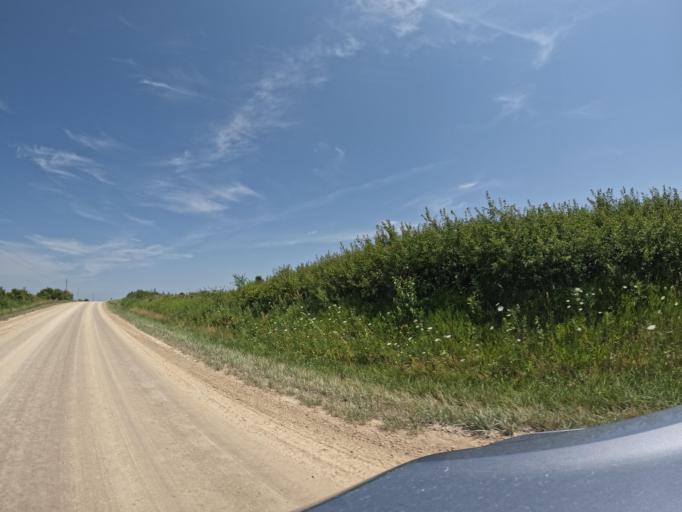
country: US
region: Iowa
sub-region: Henry County
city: Mount Pleasant
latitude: 40.9503
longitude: -91.6011
